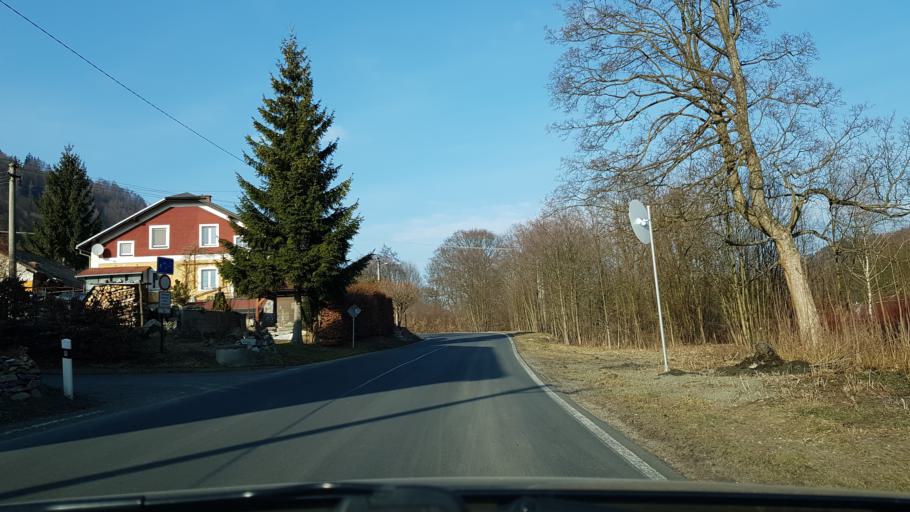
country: CZ
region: Olomoucky
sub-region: Okres Sumperk
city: Hanusovice
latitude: 50.0612
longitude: 16.9246
